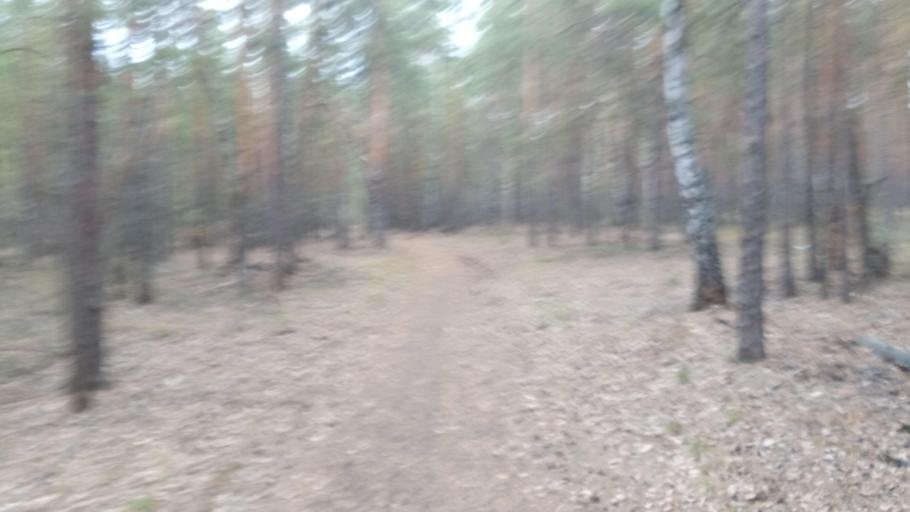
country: RU
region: Chelyabinsk
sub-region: Gorod Chelyabinsk
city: Chelyabinsk
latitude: 55.1342
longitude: 61.3391
